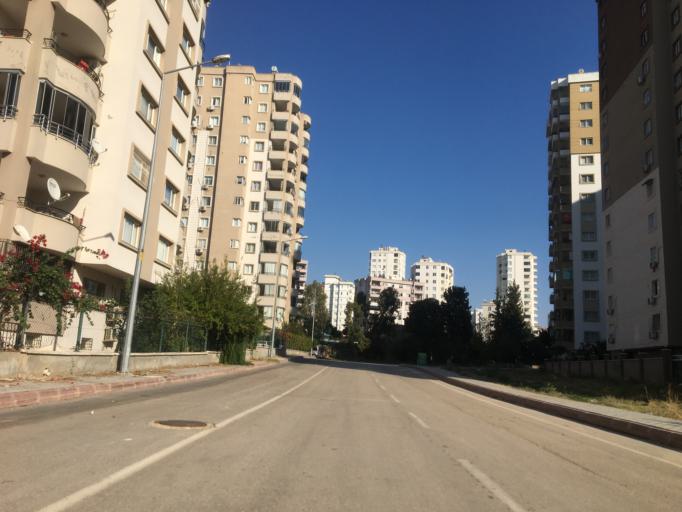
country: TR
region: Adana
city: Seyhan
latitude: 37.0284
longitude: 35.2810
